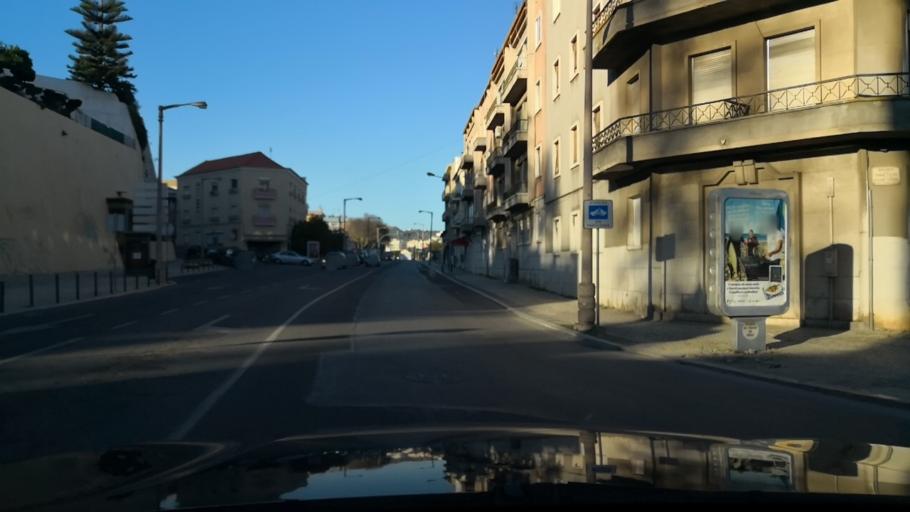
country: PT
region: Setubal
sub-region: Setubal
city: Setubal
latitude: 38.5252
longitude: -8.8986
